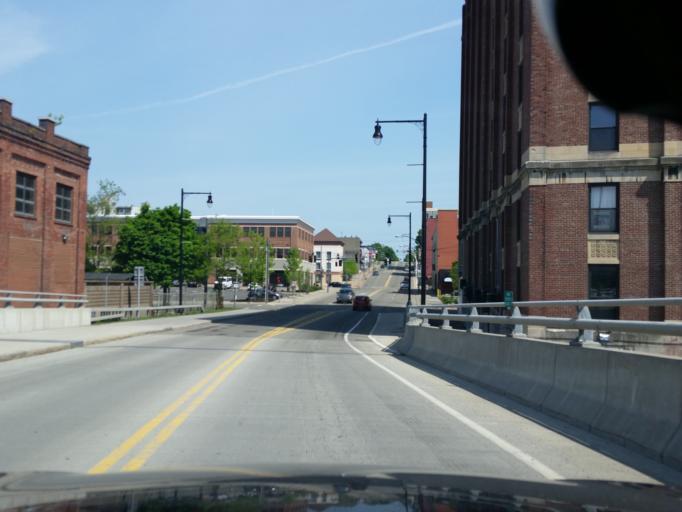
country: US
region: New York
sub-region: Chautauqua County
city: Jamestown
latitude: 42.0944
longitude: -79.2432
